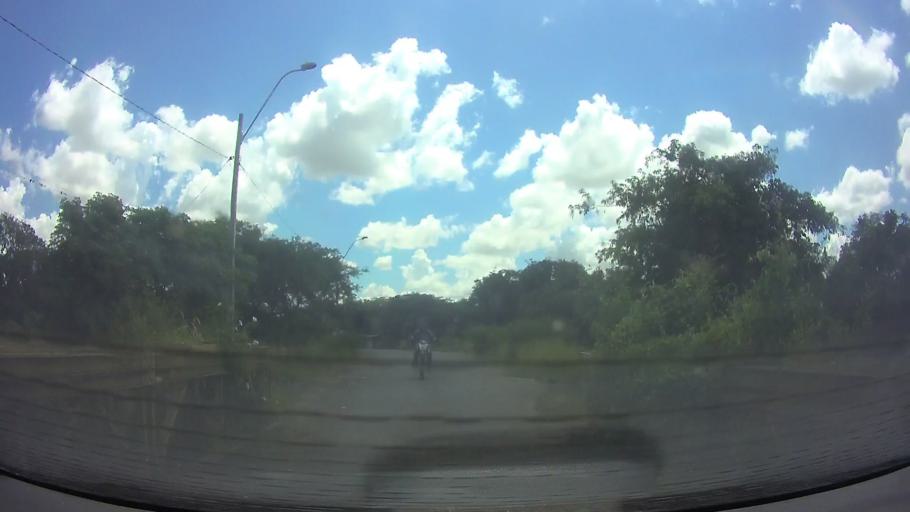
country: PY
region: Presidente Hayes
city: Nanawa
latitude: -25.2448
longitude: -57.6768
